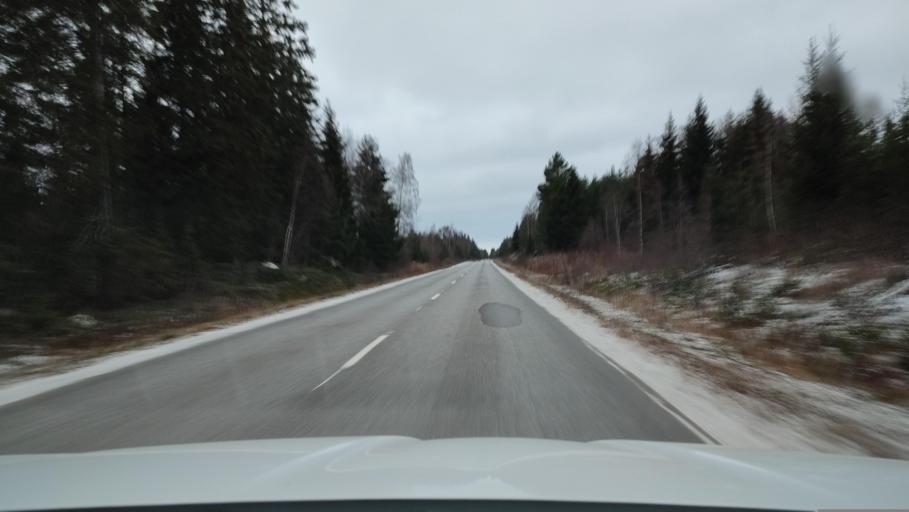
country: FI
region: Ostrobothnia
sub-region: Vaasa
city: Replot
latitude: 63.2556
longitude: 21.3683
